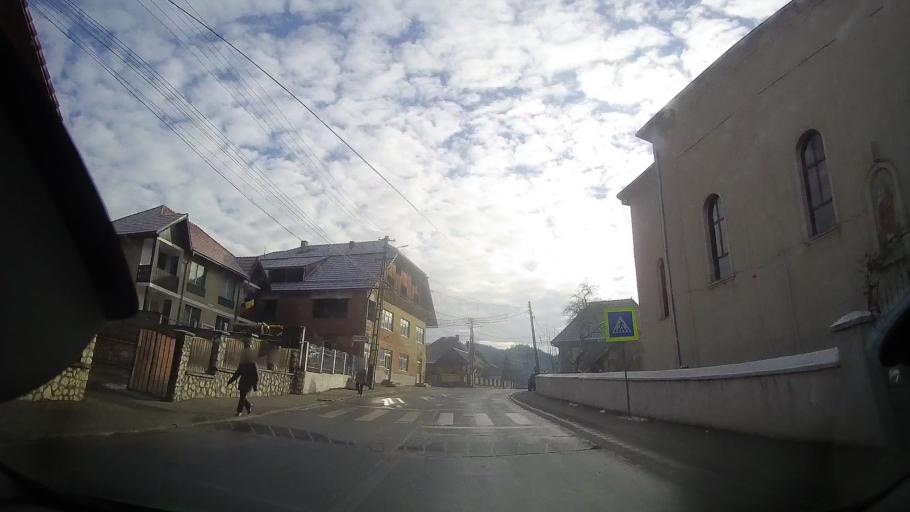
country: RO
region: Alba
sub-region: Comuna Bistra
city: Bistra
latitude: 46.3771
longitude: 23.1019
